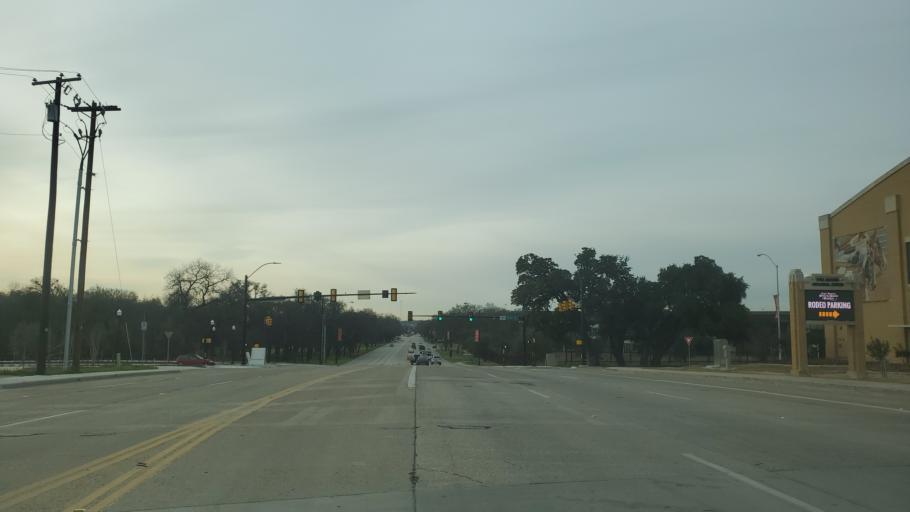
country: US
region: Texas
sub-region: Tarrant County
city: Fort Worth
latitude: 32.7438
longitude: -97.3615
